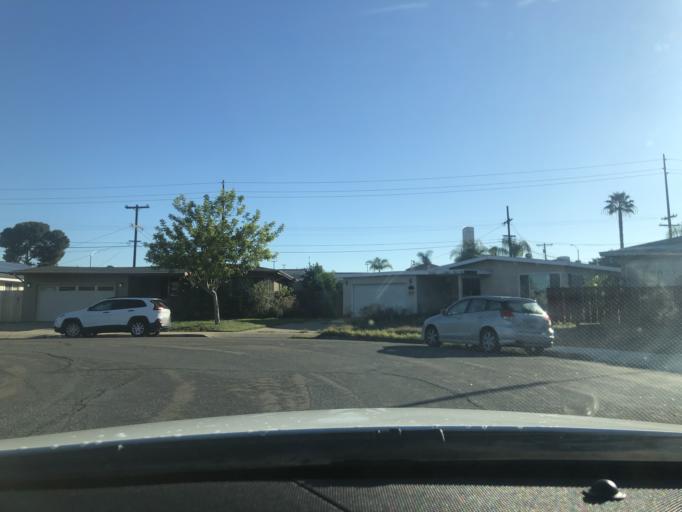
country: US
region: California
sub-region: San Diego County
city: El Cajon
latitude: 32.7812
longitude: -116.9588
